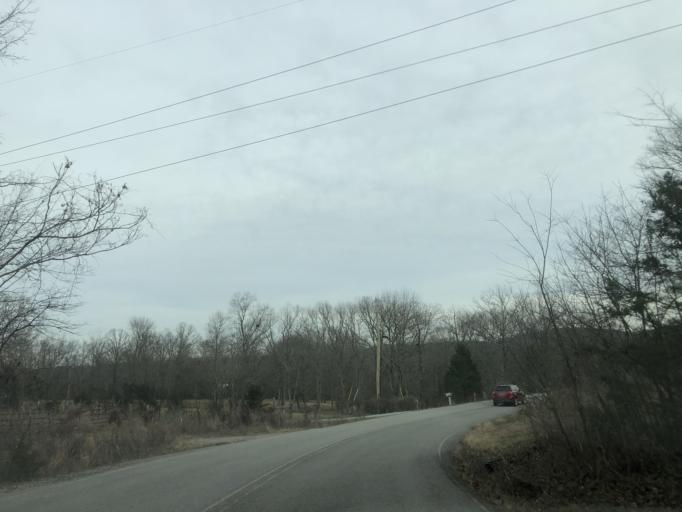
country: US
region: Tennessee
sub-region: Wilson County
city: Lebanon
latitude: 36.2558
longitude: -86.2693
